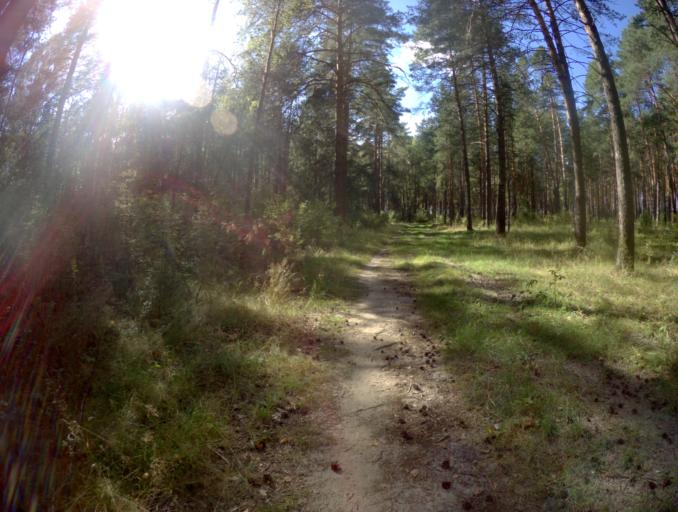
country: RU
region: Vladimir
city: Krasnaya Gorbatka
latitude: 55.8671
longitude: 41.7403
